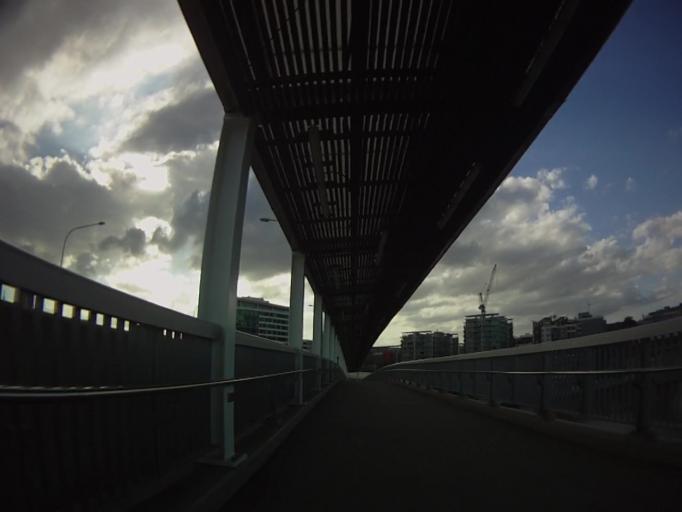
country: AU
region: Queensland
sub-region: Brisbane
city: Milton
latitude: -27.4700
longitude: 153.0126
